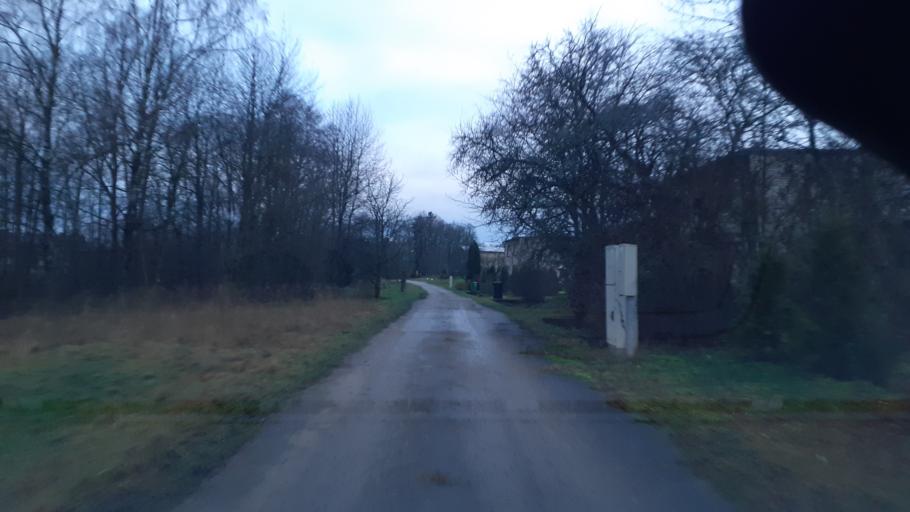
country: LV
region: Alsunga
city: Alsunga
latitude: 56.9031
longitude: 21.7014
